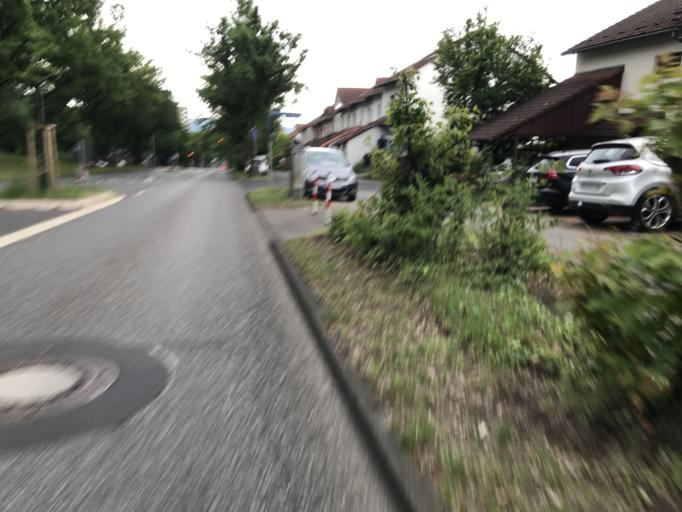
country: DE
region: Hesse
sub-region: Regierungsbezirk Kassel
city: Fuldabruck
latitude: 51.2921
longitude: 9.4470
